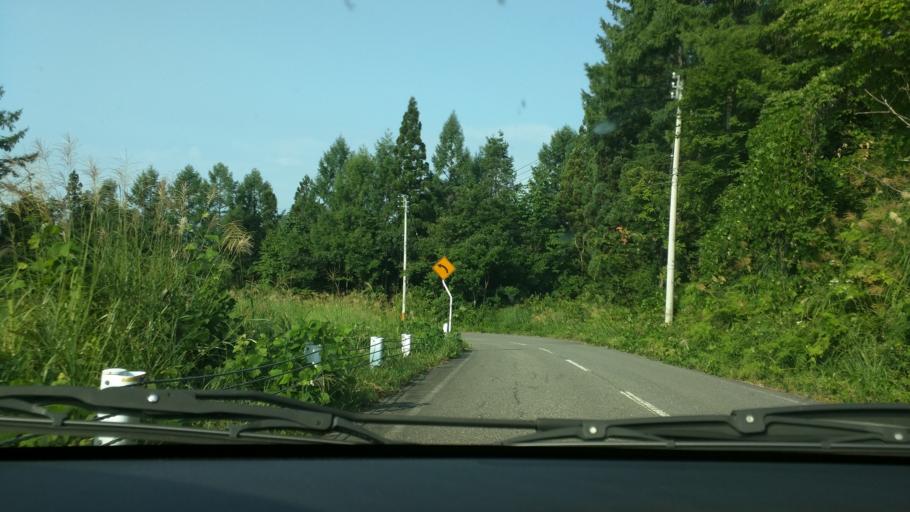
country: JP
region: Fukushima
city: Kitakata
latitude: 37.7388
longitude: 139.8703
